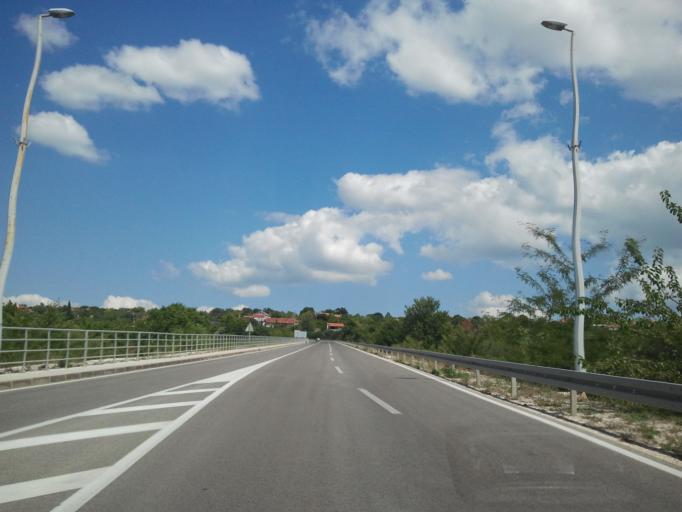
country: HR
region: Zadarska
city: Benkovac
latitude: 44.0341
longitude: 15.6175
